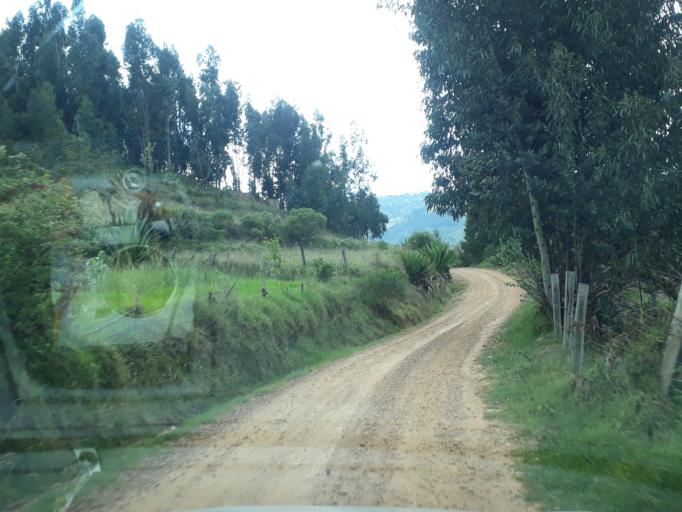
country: CO
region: Boyaca
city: Santa Rosa de Viterbo
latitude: 5.8511
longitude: -72.9598
